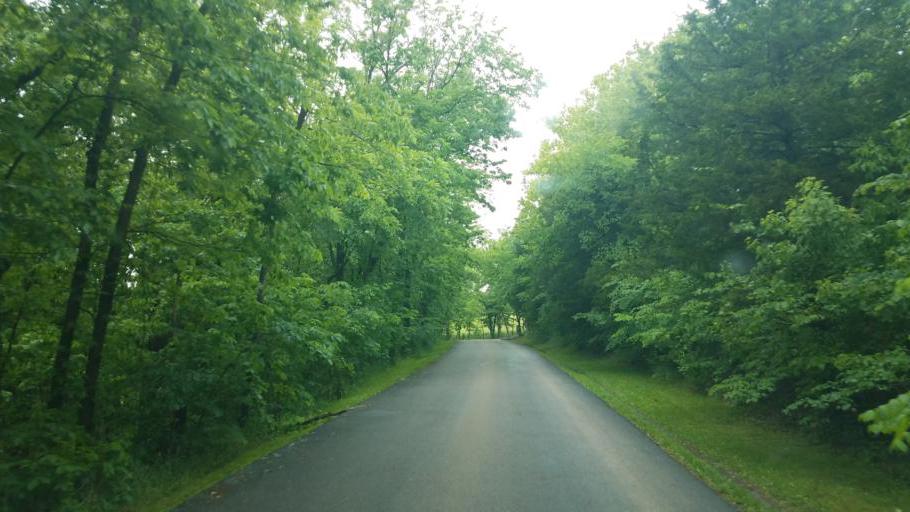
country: US
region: Missouri
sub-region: Moniteau County
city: California
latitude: 38.5907
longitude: -92.5706
